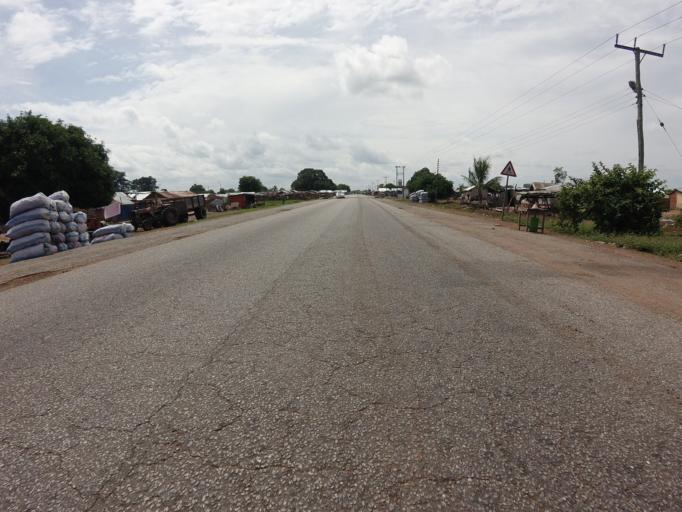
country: GH
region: Brong-Ahafo
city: Kintampo
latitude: 8.4467
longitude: -1.5648
